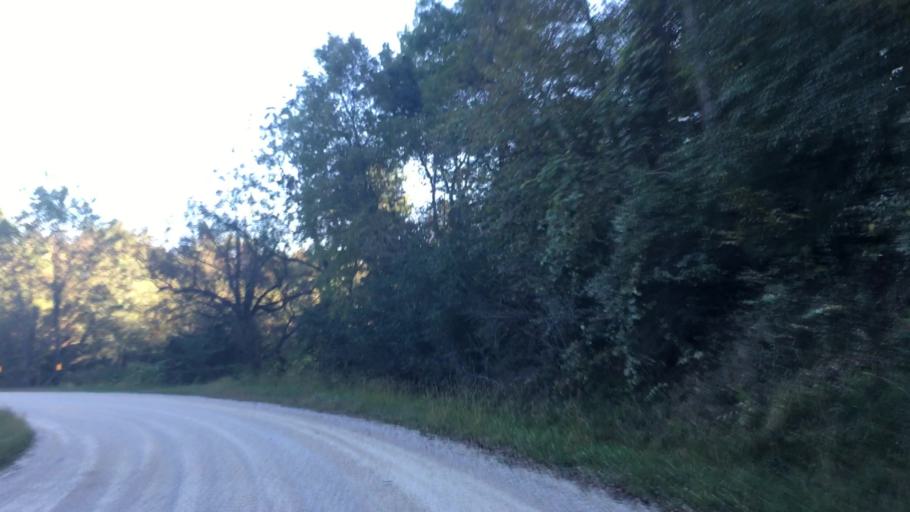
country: US
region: Minnesota
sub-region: Fillmore County
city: Preston
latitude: 43.7823
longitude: -92.0380
